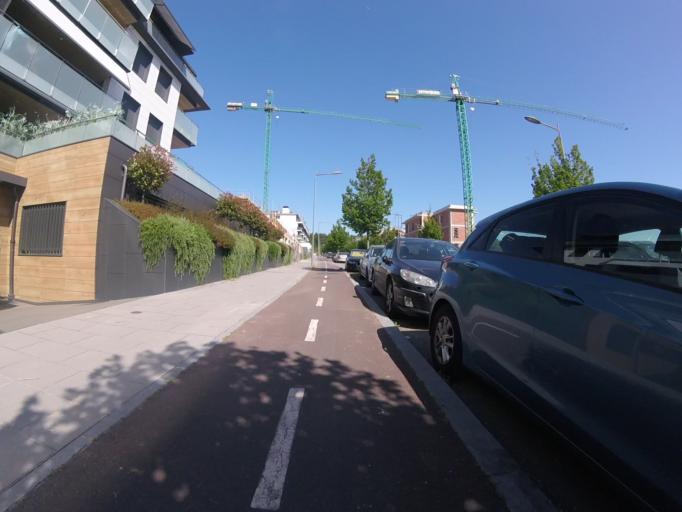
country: ES
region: Basque Country
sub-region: Provincia de Guipuzcoa
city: San Sebastian
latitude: 43.2985
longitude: -1.9974
